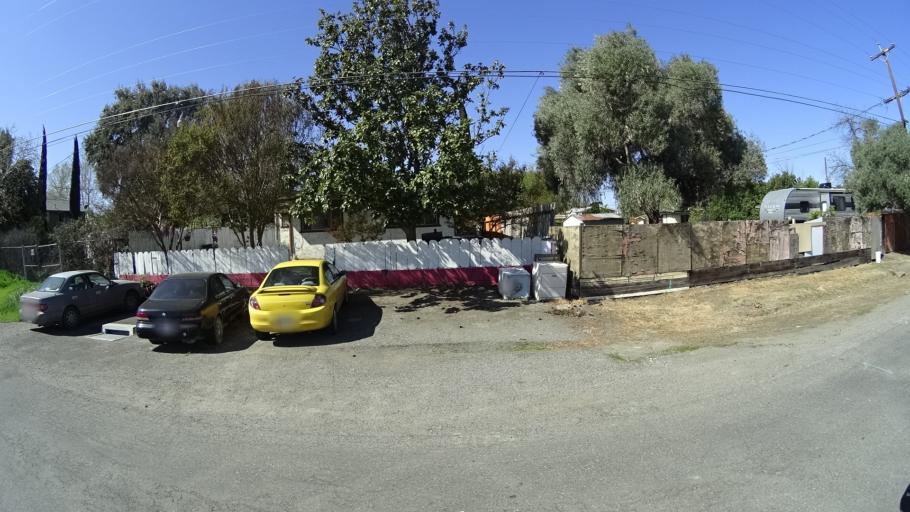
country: US
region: California
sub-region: Glenn County
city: Hamilton City
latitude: 39.7426
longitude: -122.0115
